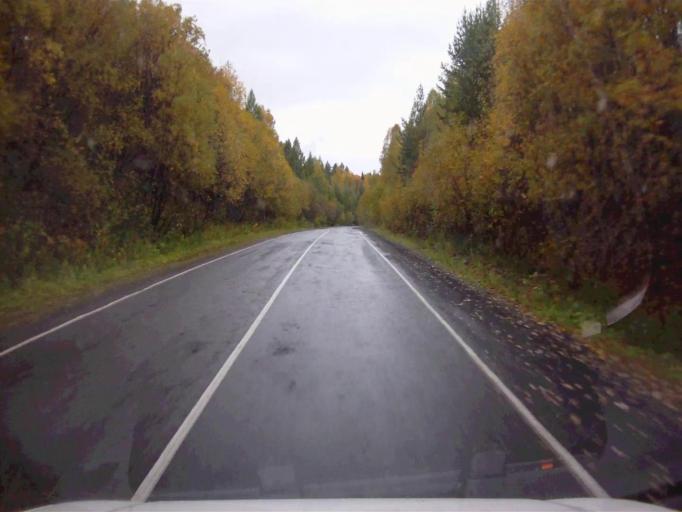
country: RU
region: Chelyabinsk
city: Verkhniy Ufaley
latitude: 56.0437
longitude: 60.1068
